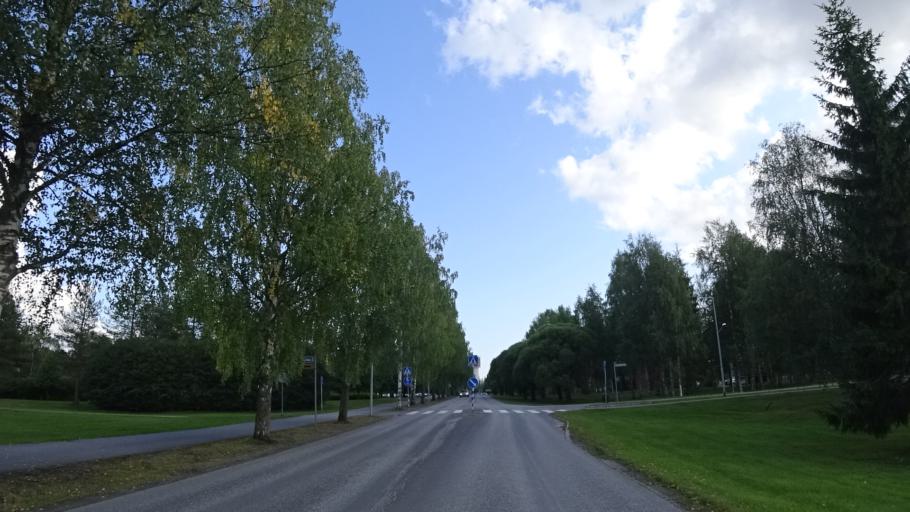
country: FI
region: North Karelia
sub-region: Pielisen Karjala
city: Lieksa
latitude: 63.3274
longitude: 30.0224
